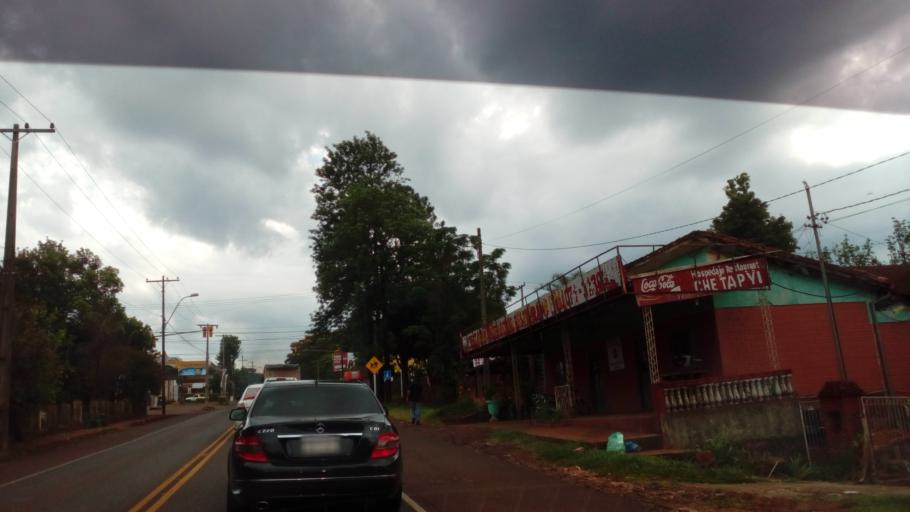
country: PY
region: Itapua
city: Obligado
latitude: -27.0853
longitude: -55.6508
